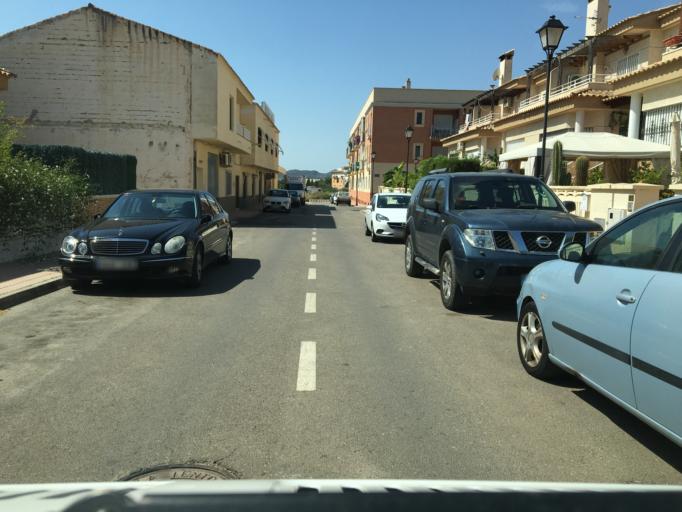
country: ES
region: Andalusia
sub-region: Provincia de Almeria
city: Huercal-Overa
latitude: 37.3981
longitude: -1.9380
